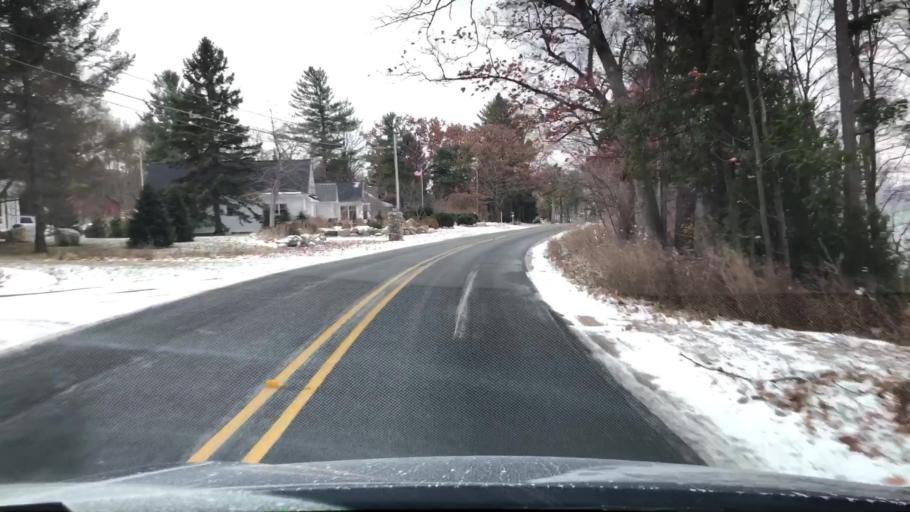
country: US
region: Michigan
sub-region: Grand Traverse County
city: Traverse City
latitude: 44.8127
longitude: -85.5787
